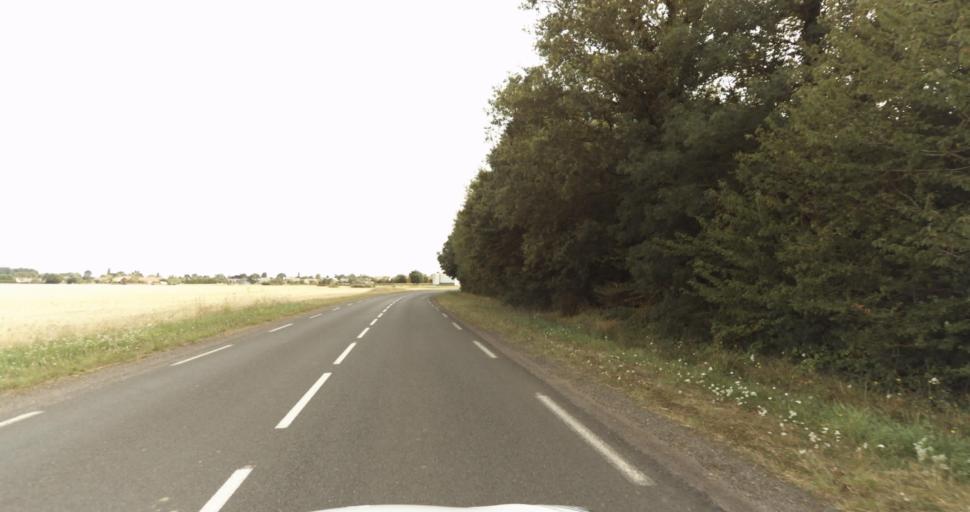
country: FR
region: Haute-Normandie
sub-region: Departement de l'Eure
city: La Madeleine-de-Nonancourt
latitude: 48.8543
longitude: 1.2441
